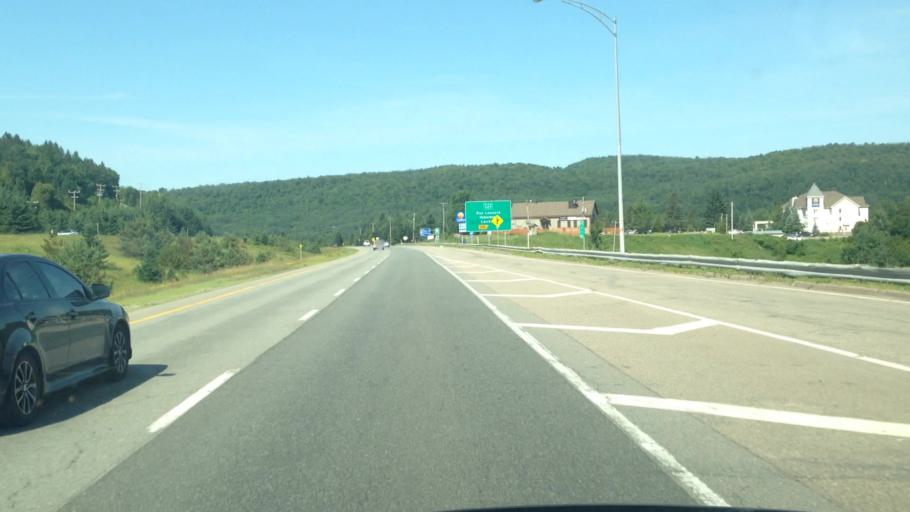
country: CA
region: Quebec
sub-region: Laurentides
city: Mont-Tremblant
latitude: 46.1149
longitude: -74.5874
